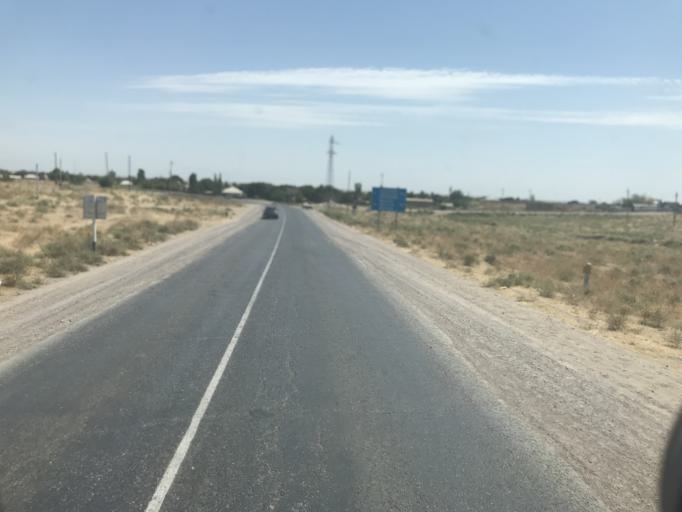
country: UZ
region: Toshkent
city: Yangiyul
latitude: 41.3291
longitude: 68.8914
